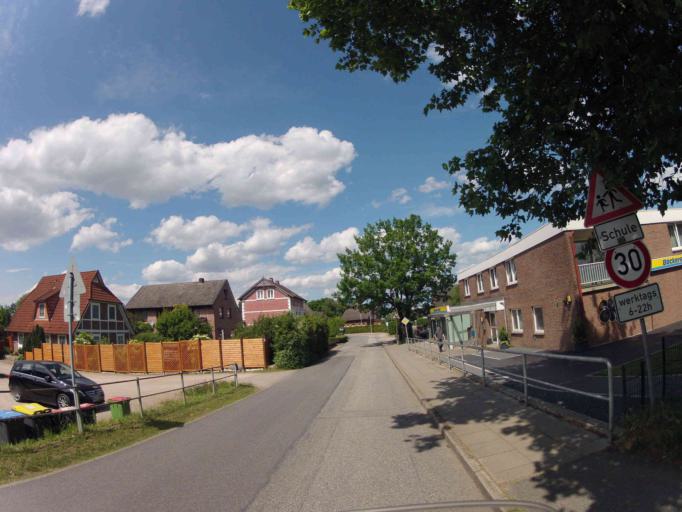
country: DE
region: Lower Saxony
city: Winsen
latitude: 53.3989
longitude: 10.1829
